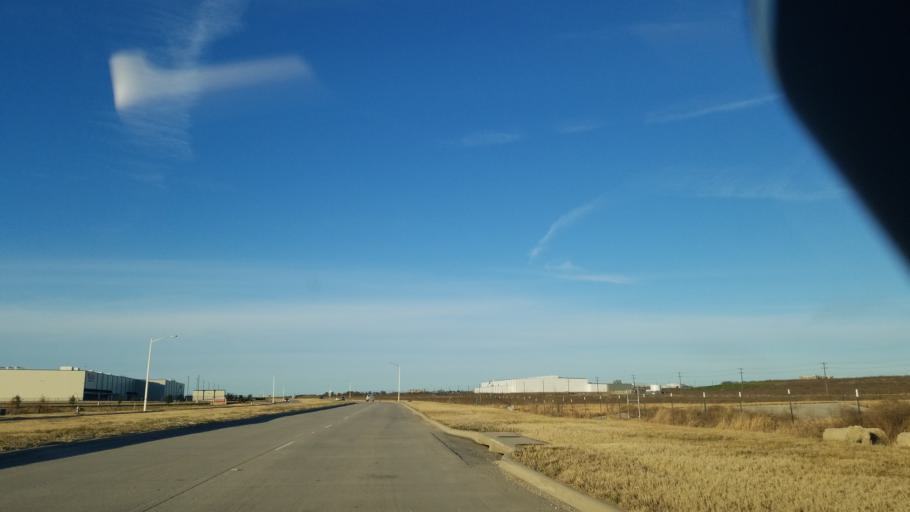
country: US
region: Texas
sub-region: Denton County
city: Denton
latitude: 33.2080
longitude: -97.1847
